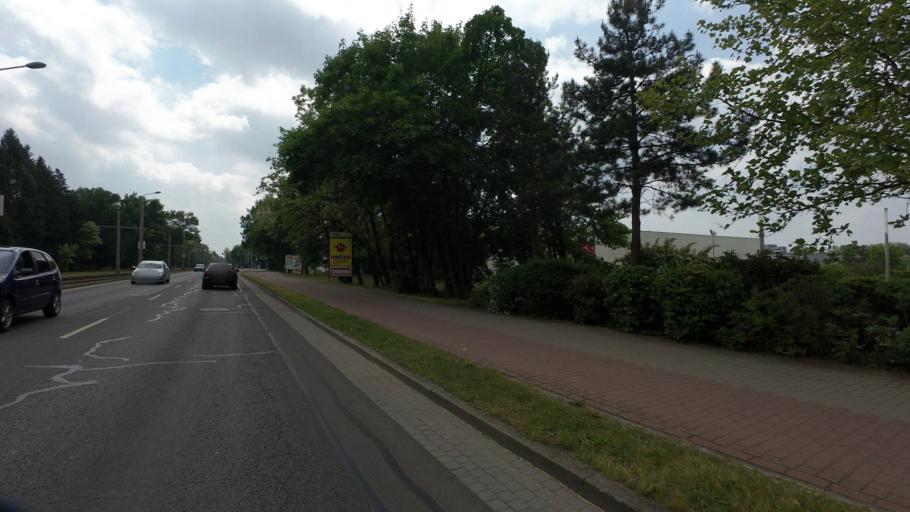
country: DE
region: Brandenburg
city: Cottbus
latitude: 51.7362
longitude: 14.3366
